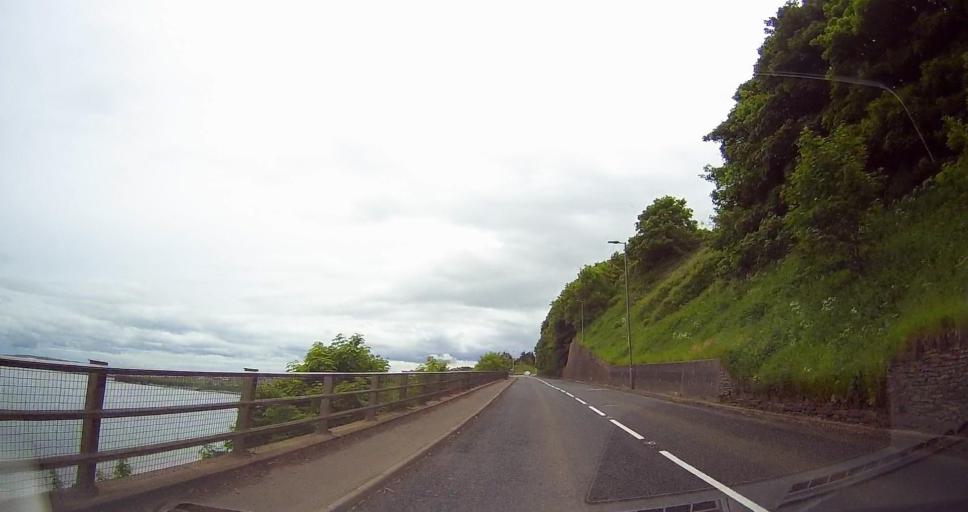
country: GB
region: Scotland
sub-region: Highland
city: Thurso
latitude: 58.6086
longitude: -3.5523
